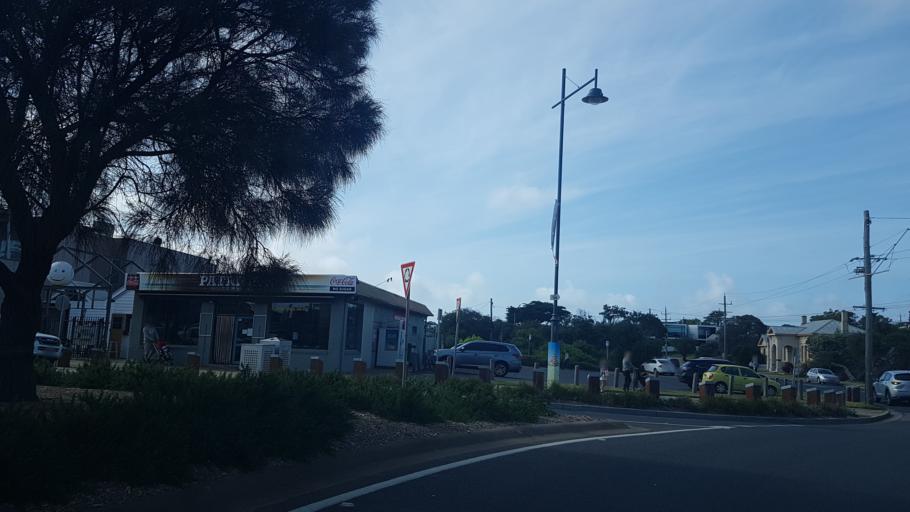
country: AU
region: Victoria
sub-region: Mornington Peninsula
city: Sorrento
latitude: -38.3399
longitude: 144.7366
